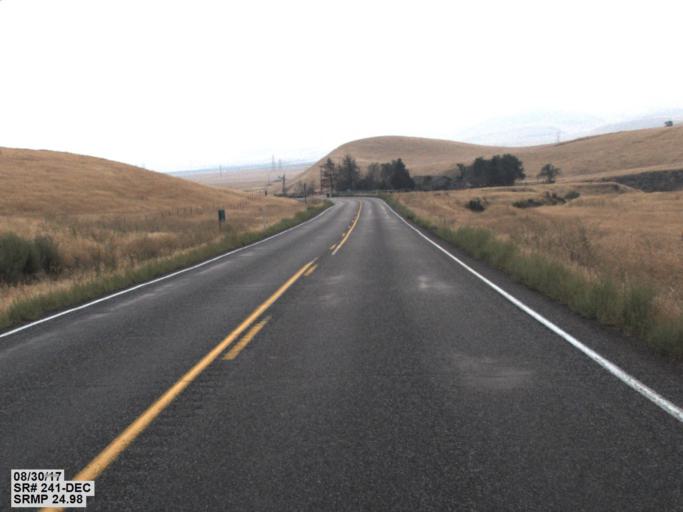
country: US
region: Washington
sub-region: Grant County
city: Desert Aire
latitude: 46.5310
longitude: -119.8791
